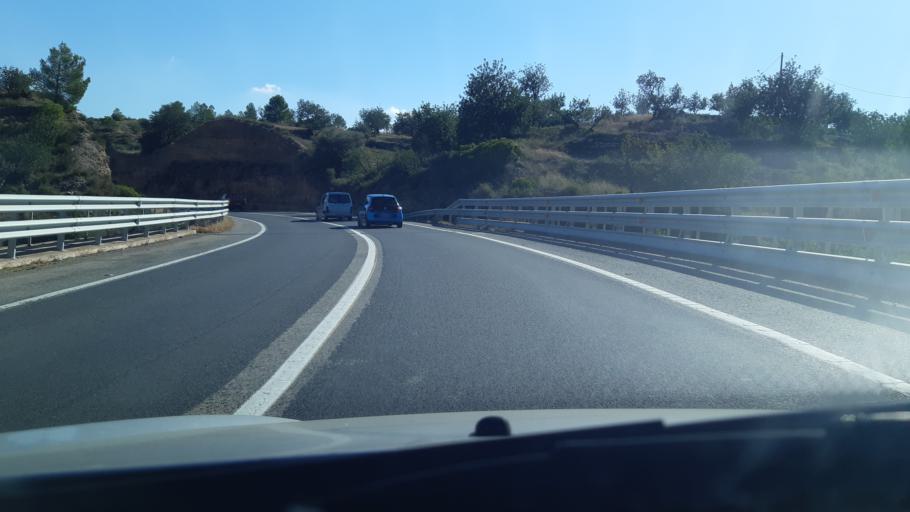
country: ES
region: Catalonia
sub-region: Provincia de Tarragona
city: Tivenys
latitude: 40.8792
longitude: 0.4975
